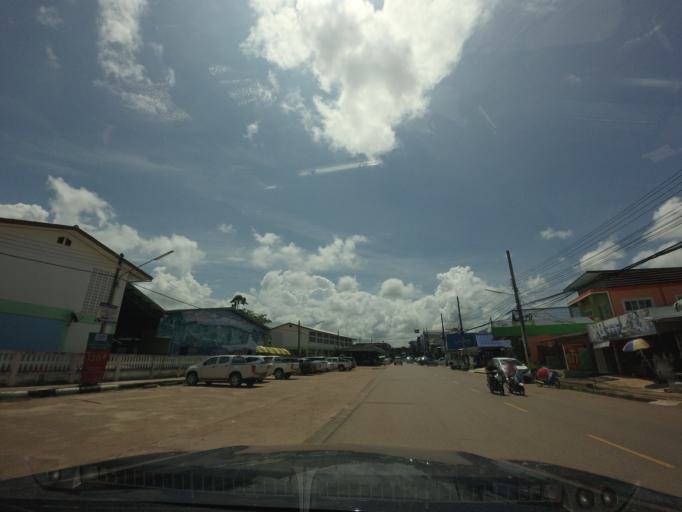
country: TH
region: Changwat Udon Thani
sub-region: Amphoe Ban Phue
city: Ban Phue
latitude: 17.6902
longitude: 102.4665
